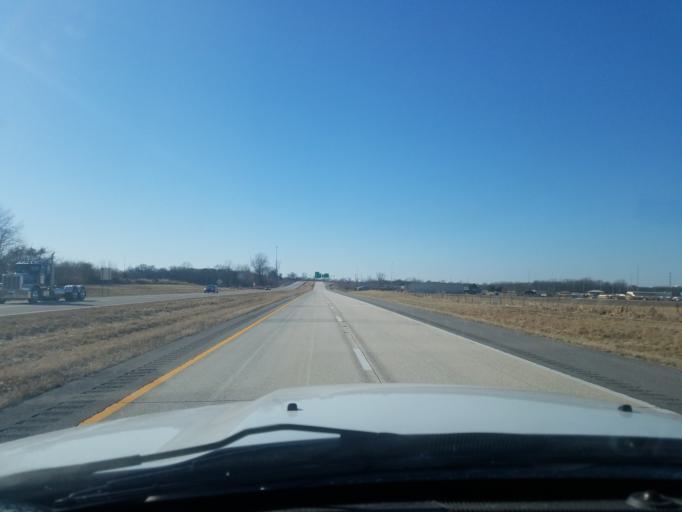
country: US
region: Kentucky
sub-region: Henderson County
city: Henderson
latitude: 37.8095
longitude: -87.5544
